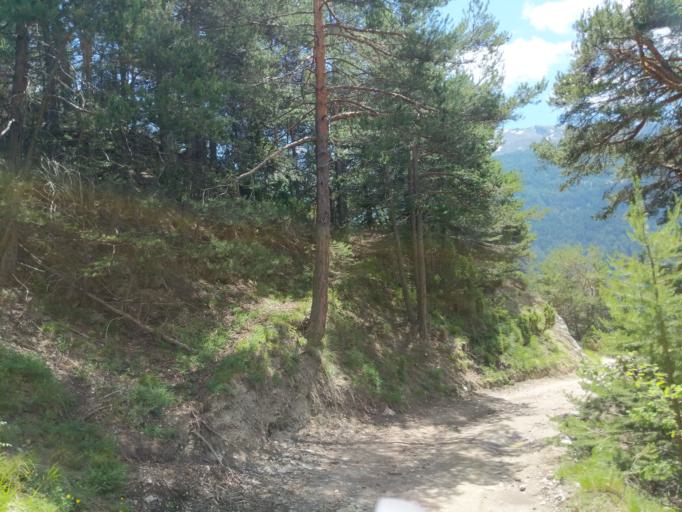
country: FR
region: Rhone-Alpes
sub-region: Departement de la Savoie
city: Modane
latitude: 45.2243
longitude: 6.7498
